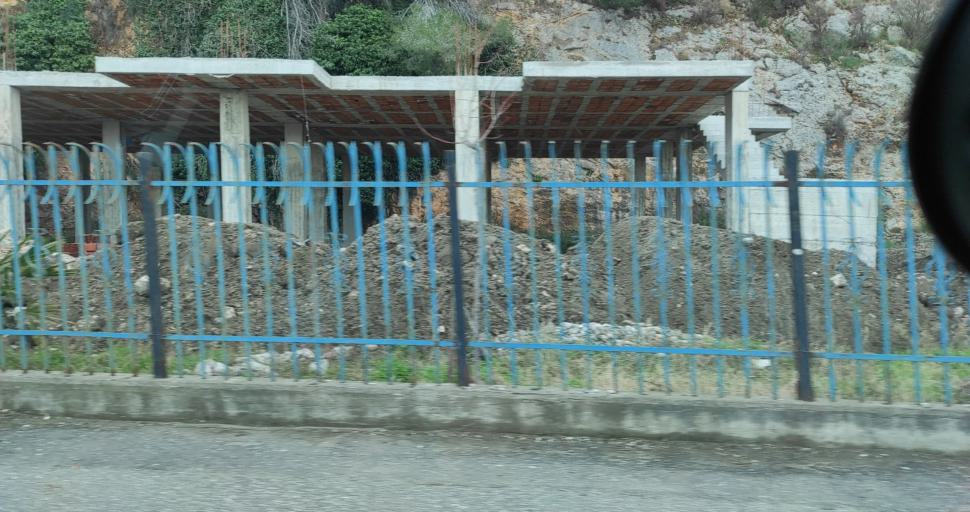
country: AL
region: Lezhe
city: Shengjin
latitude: 41.7990
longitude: 19.6179
